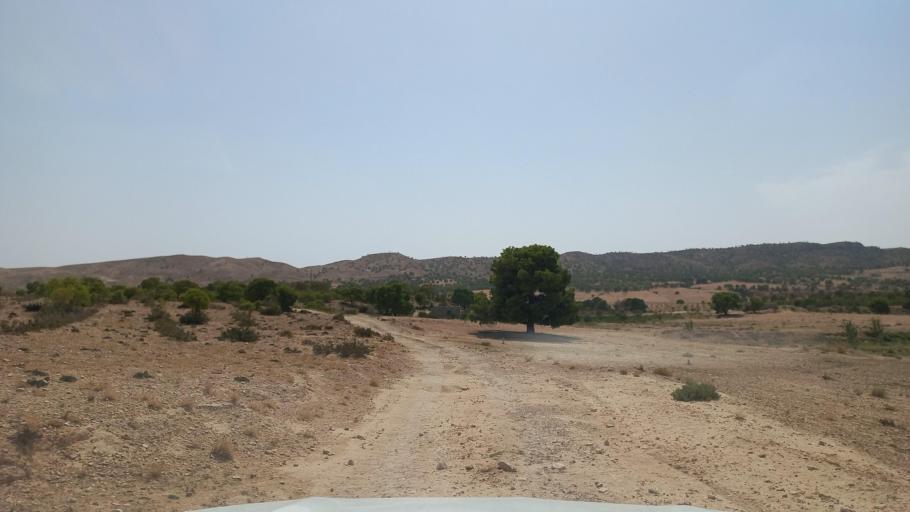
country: TN
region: Al Qasrayn
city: Sbiba
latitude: 35.3953
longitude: 8.9860
